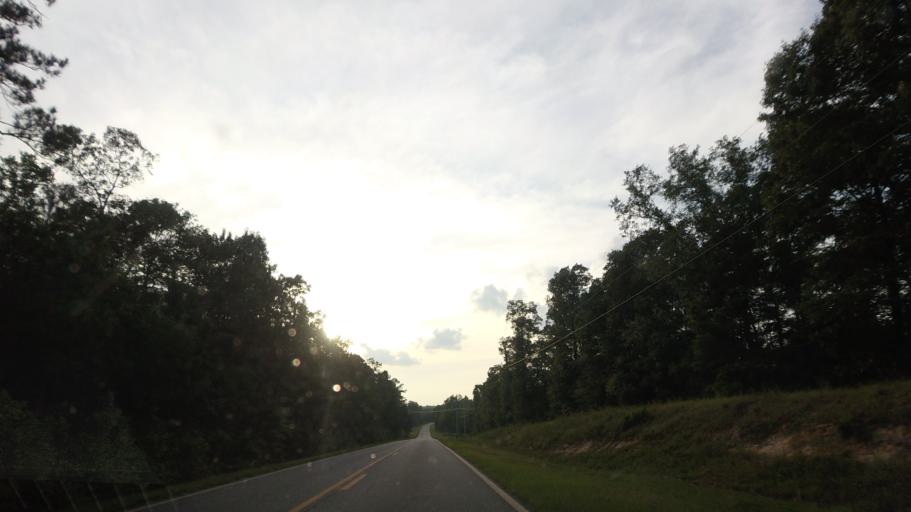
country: US
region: Georgia
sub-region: Wilkinson County
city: Gordon
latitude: 32.8570
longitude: -83.4468
